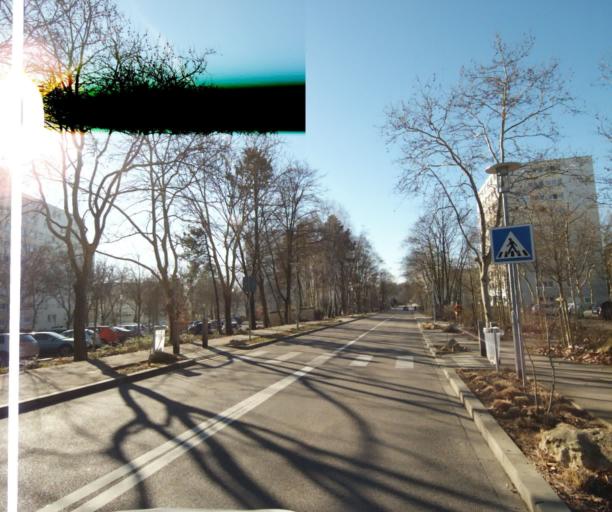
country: FR
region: Lorraine
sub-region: Departement de Meurthe-et-Moselle
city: Laxou
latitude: 48.7022
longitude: 6.1304
